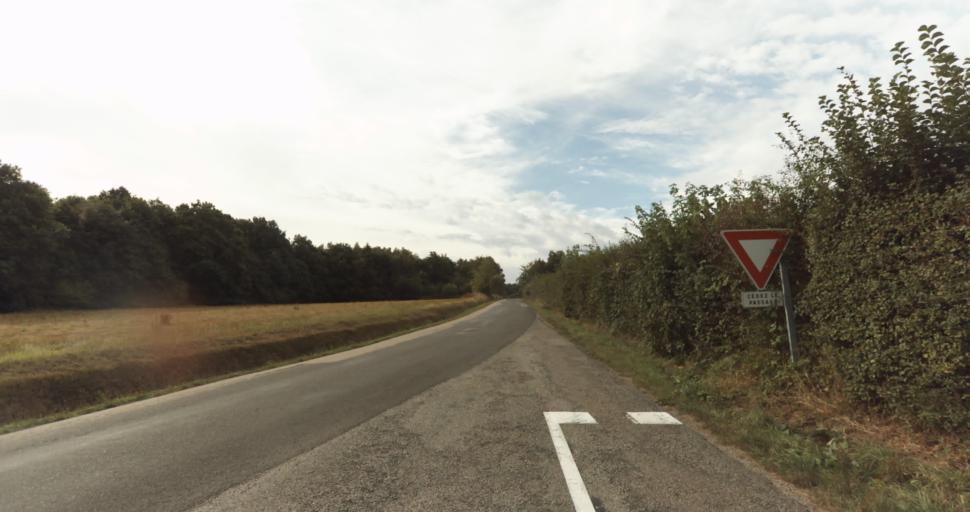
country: FR
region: Lower Normandy
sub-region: Departement de l'Orne
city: Vimoutiers
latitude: 48.9237
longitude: 0.2486
